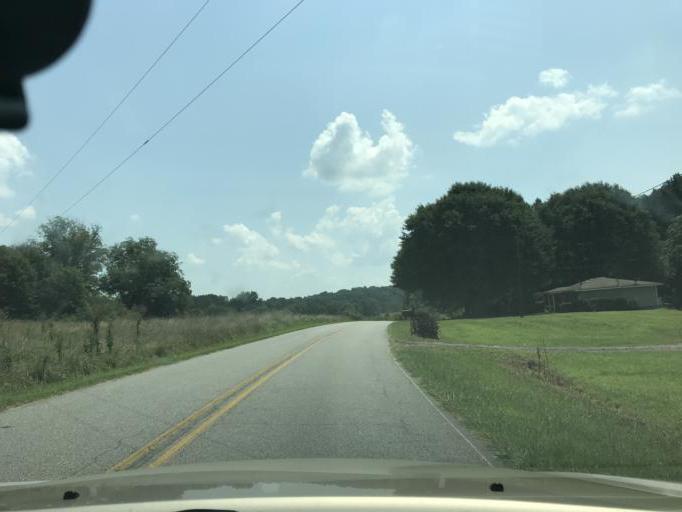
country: US
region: Georgia
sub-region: Forsyth County
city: Cumming
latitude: 34.3105
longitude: -84.1099
